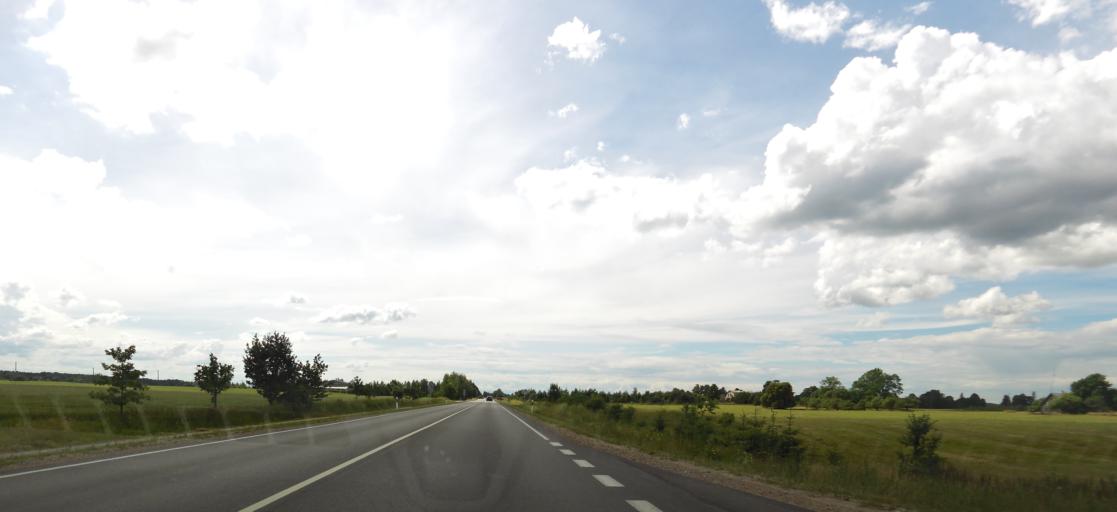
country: LT
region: Panevezys
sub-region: Birzai
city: Birzai
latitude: 56.1970
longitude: 24.7043
